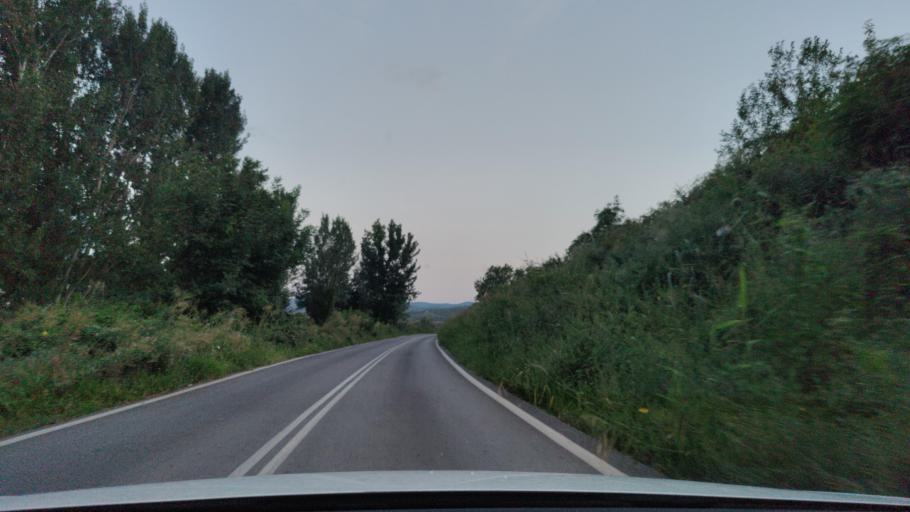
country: GR
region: Central Macedonia
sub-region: Nomos Serron
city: Chrysochorafa
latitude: 41.1421
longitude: 23.2287
